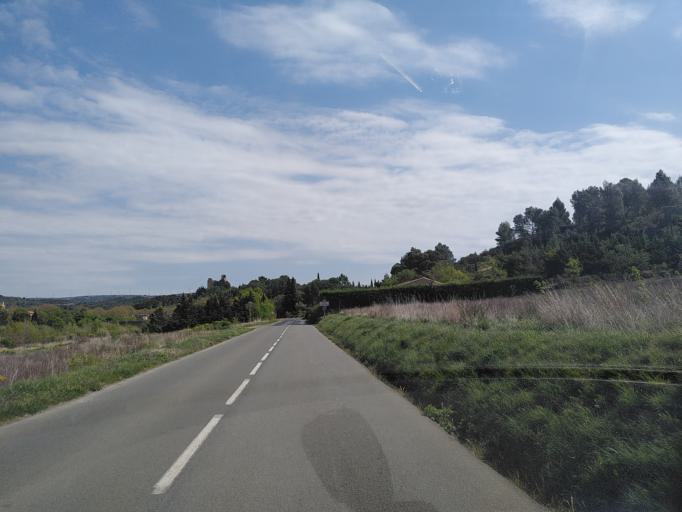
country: FR
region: Languedoc-Roussillon
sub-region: Departement de l'Aude
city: Portel-des-Corbieres
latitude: 42.9922
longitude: 2.8076
